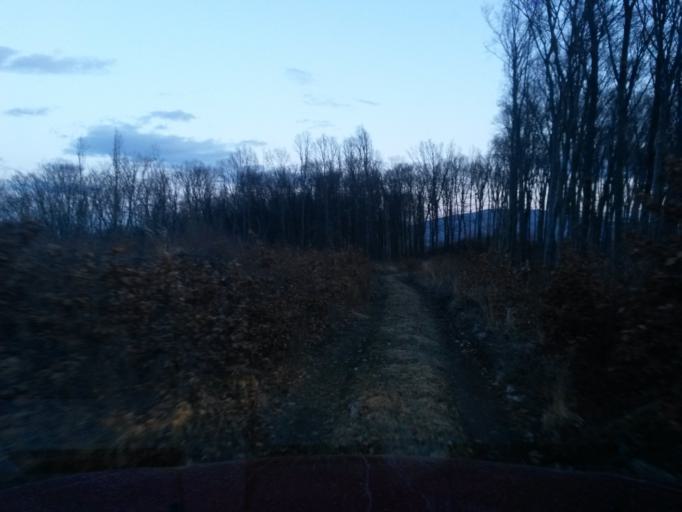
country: SK
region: Kosicky
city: Kosice
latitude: 48.7021
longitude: 21.3836
